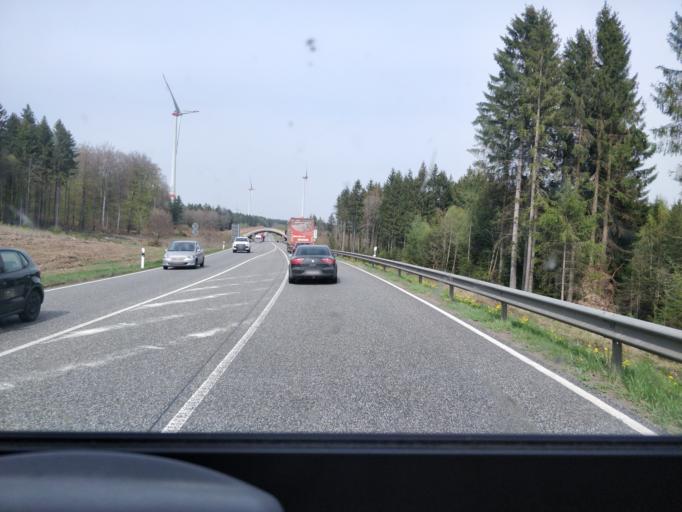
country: DE
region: Rheinland-Pfalz
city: Reuth
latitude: 50.3128
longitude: 6.4971
